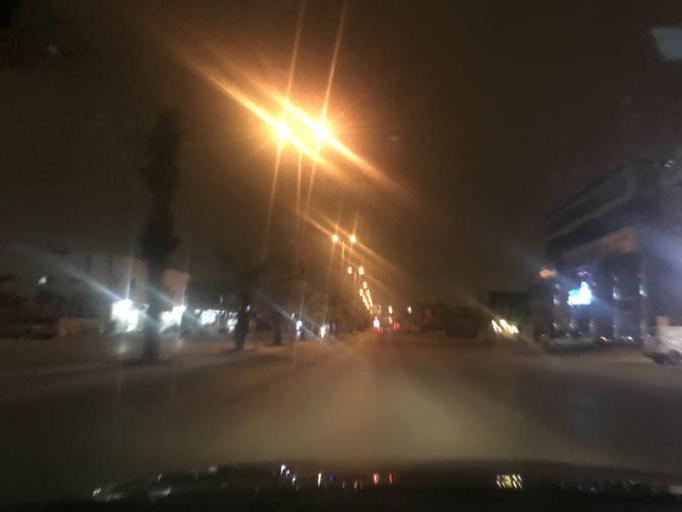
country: SA
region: Ar Riyad
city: Riyadh
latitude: 24.7504
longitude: 46.7796
